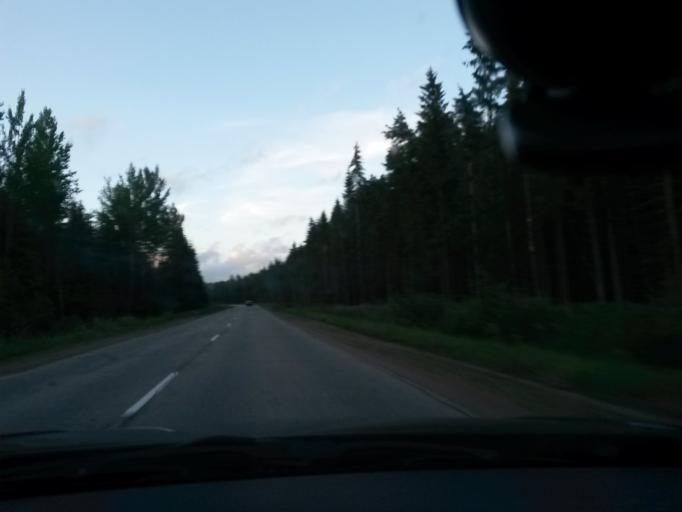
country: LV
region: Jekabpils Rajons
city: Jekabpils
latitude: 56.6731
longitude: 25.9771
